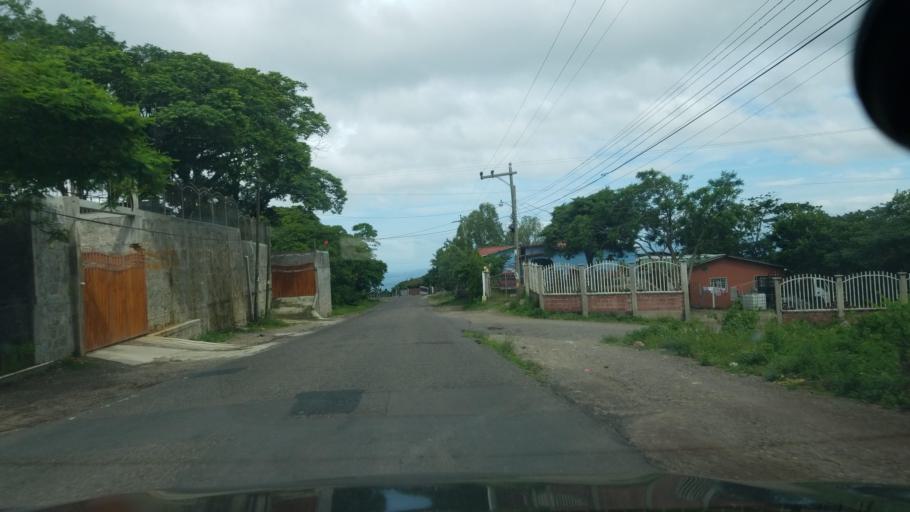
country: HN
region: Choluteca
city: Corpus
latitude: 13.3713
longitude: -86.9668
